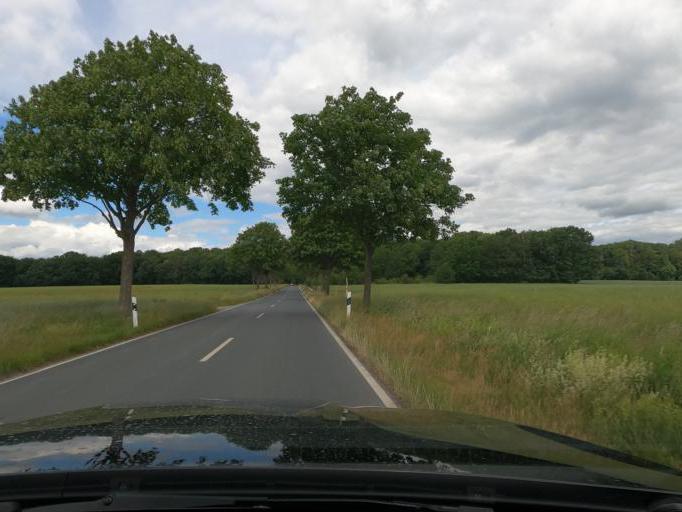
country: DE
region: Lower Saxony
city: Lehrte
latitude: 52.3868
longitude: 9.9235
